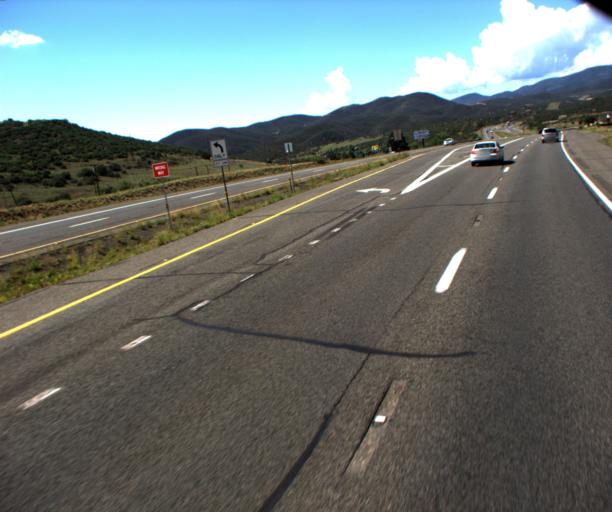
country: US
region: Arizona
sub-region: Yavapai County
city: Dewey-Humboldt
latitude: 34.4940
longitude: -112.2488
